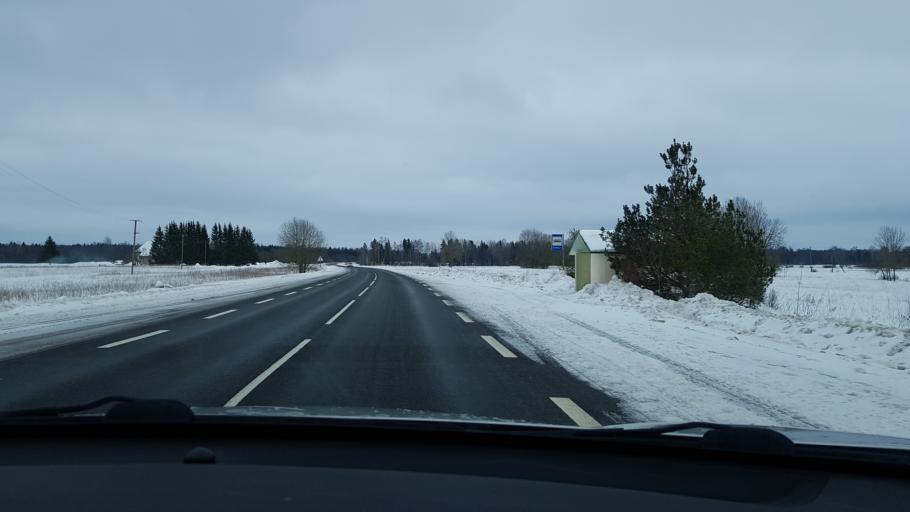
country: EE
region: Jaervamaa
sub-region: Jaerva-Jaani vald
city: Jarva-Jaani
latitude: 59.0829
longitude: 25.8409
